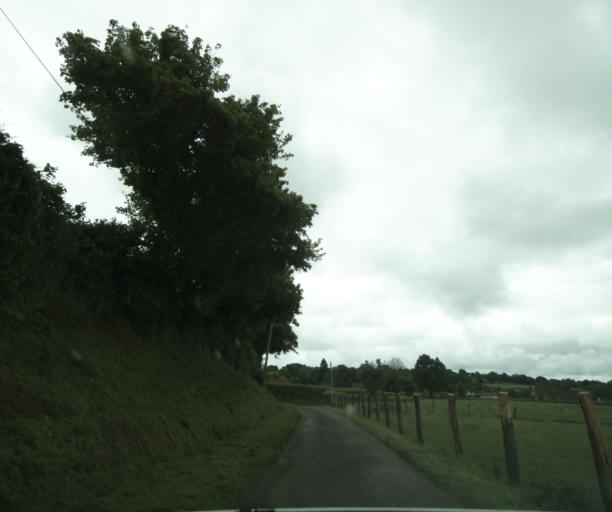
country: FR
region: Bourgogne
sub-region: Departement de Saone-et-Loire
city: Charolles
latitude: 46.4762
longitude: 4.3342
